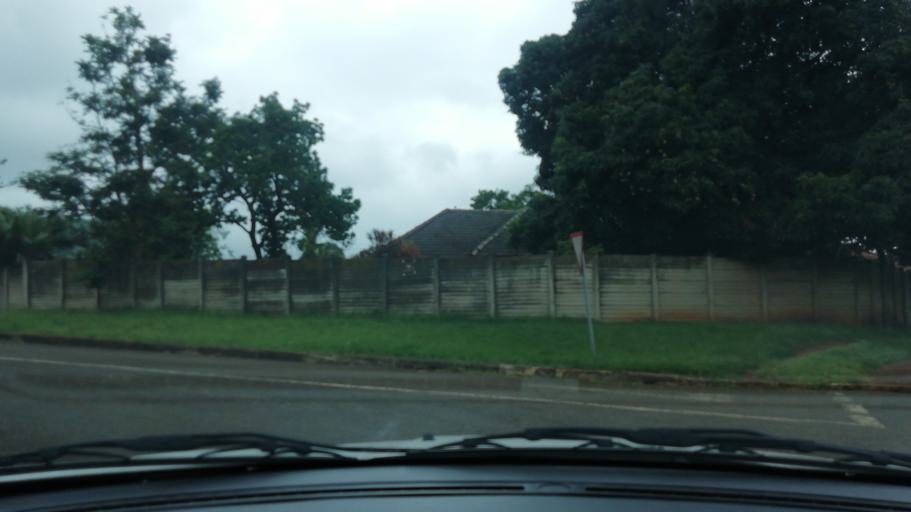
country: ZA
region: KwaZulu-Natal
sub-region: uThungulu District Municipality
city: Empangeni
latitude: -28.7614
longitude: 31.9011
